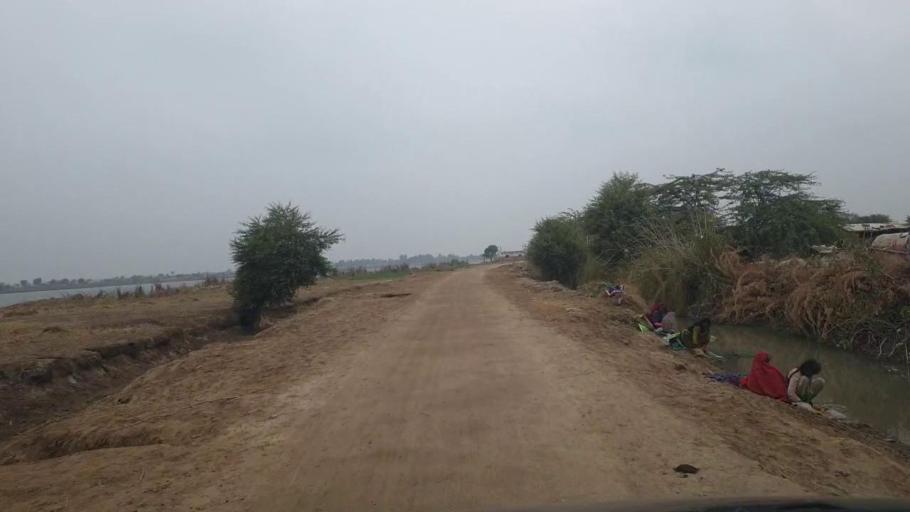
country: PK
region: Sindh
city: Tando Adam
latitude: 25.8481
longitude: 68.6994
